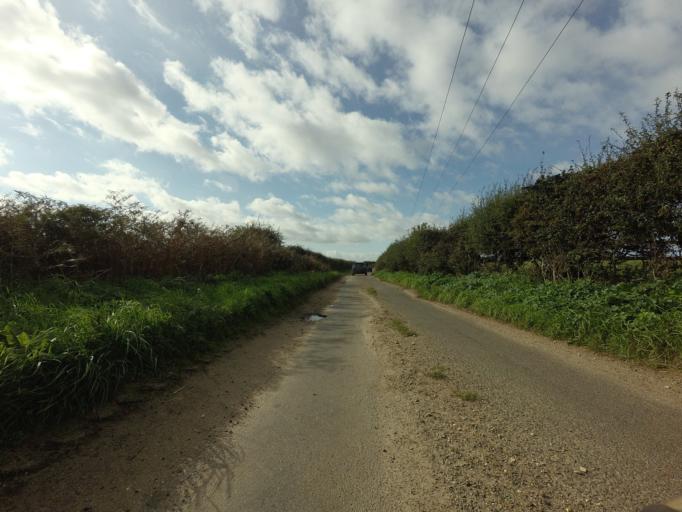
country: GB
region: England
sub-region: Norfolk
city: Hunstanton
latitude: 52.9357
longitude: 0.6487
